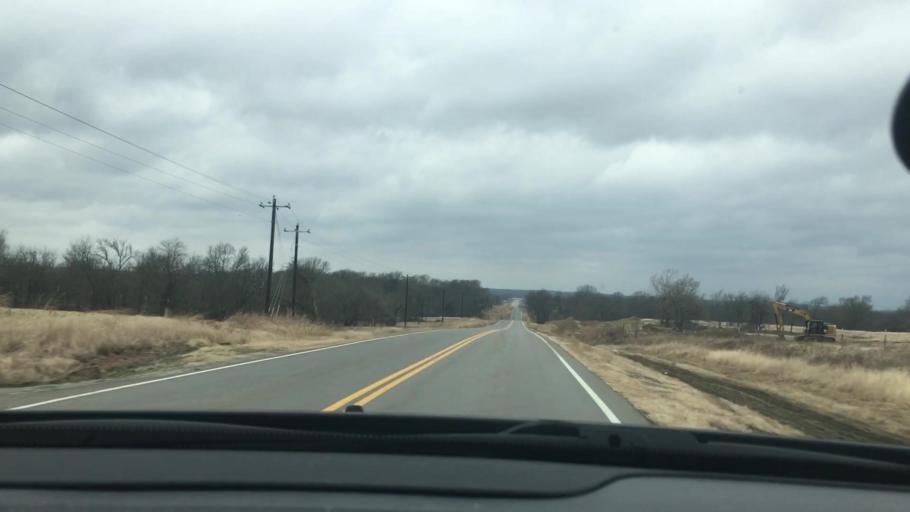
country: US
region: Oklahoma
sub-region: Atoka County
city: Atoka
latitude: 34.3778
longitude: -96.2925
